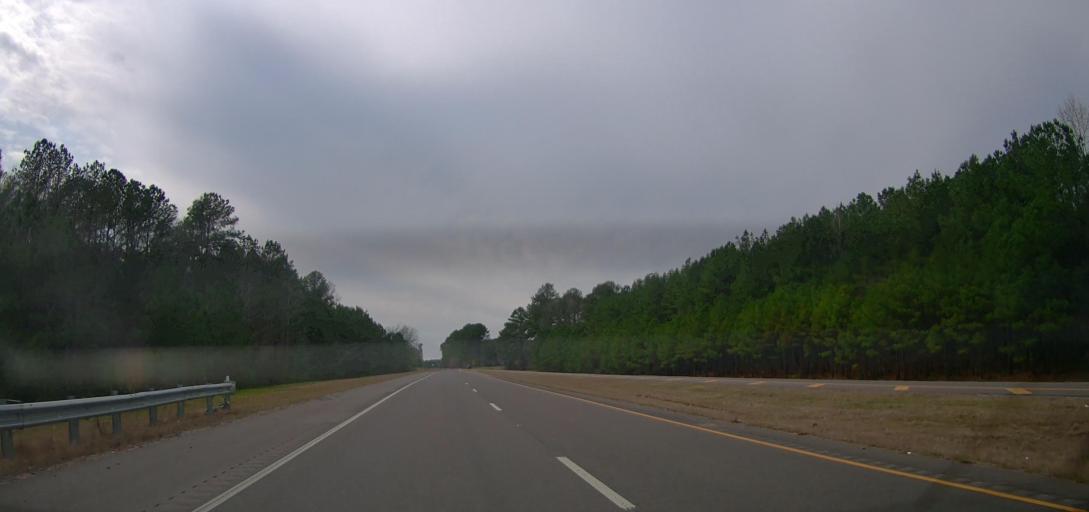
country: US
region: Alabama
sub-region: Walker County
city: Carbon Hill
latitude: 33.8723
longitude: -87.4511
